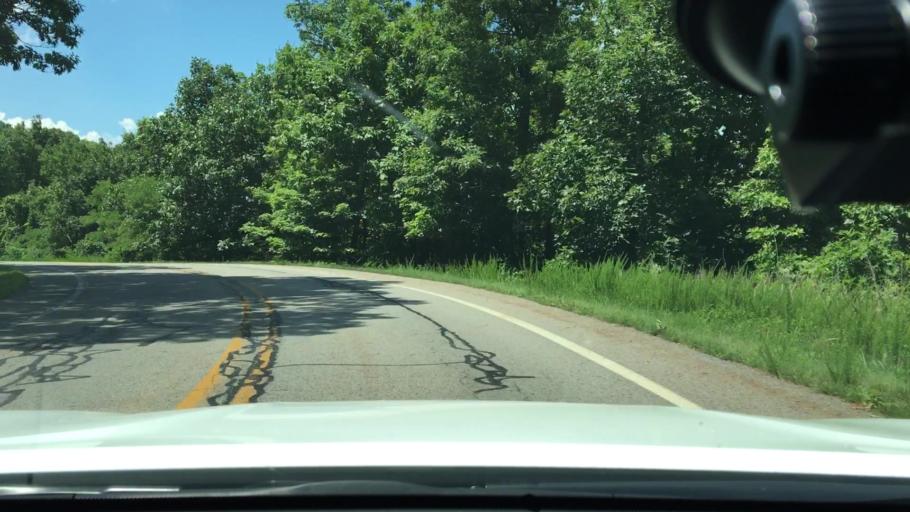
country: US
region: Arkansas
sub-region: Logan County
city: Paris
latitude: 35.1695
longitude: -93.6345
